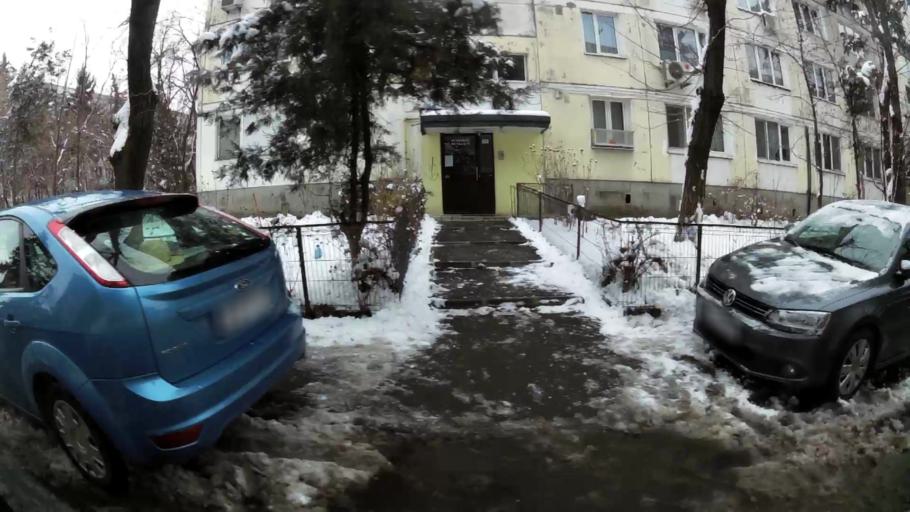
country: RO
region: Bucuresti
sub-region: Municipiul Bucuresti
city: Bucuresti
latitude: 44.3943
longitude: 26.1004
